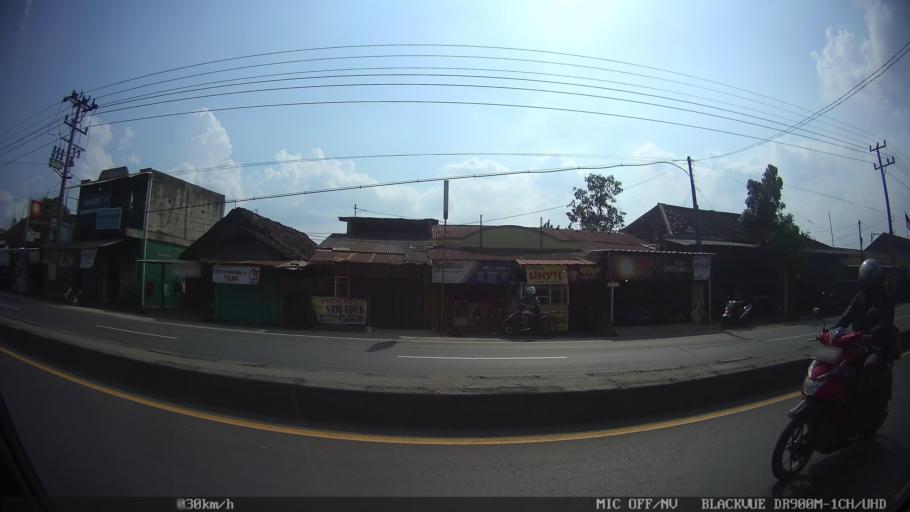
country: ID
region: Lampung
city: Natar
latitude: -5.3160
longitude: 105.1965
